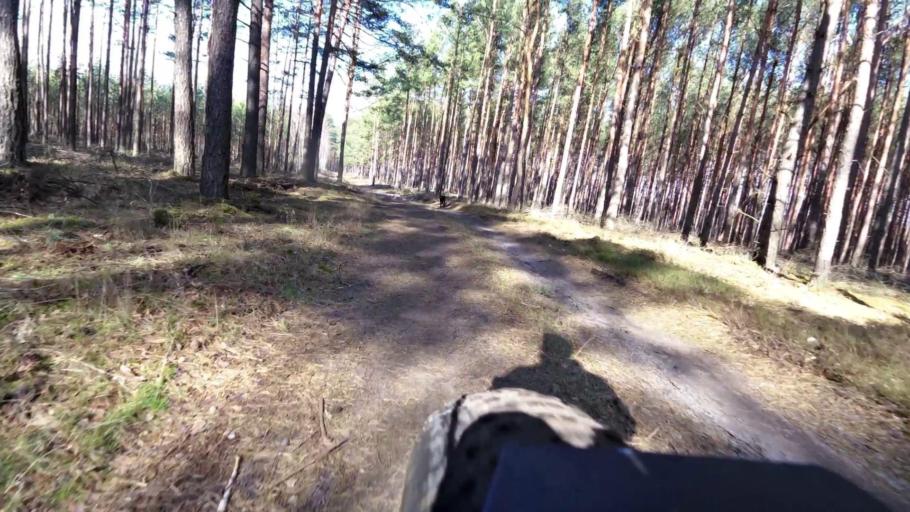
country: PL
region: Lubusz
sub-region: Powiat sulecinski
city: Torzym
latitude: 52.2198
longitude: 14.9898
